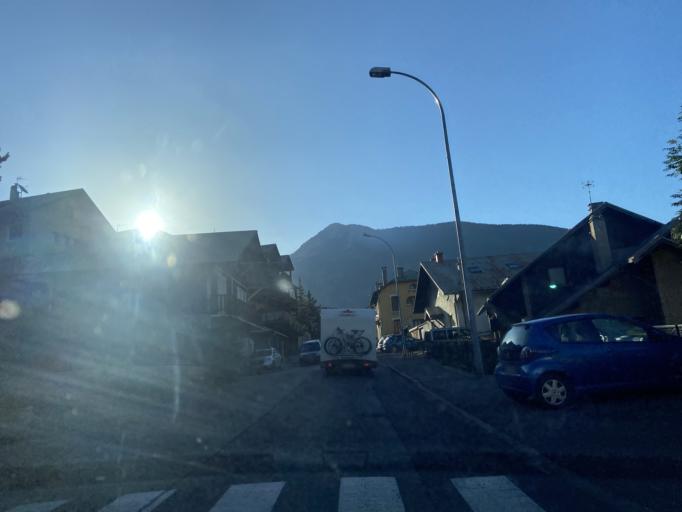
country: FR
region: Provence-Alpes-Cote d'Azur
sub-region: Departement des Hautes-Alpes
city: Briancon
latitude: 44.9020
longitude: 6.6406
